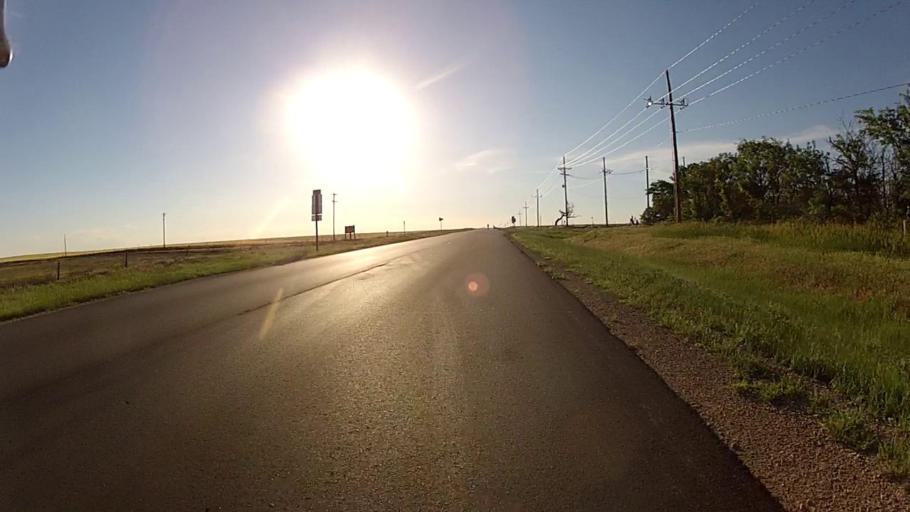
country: US
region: Kansas
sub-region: Comanche County
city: Coldwater
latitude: 37.2816
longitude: -99.1662
